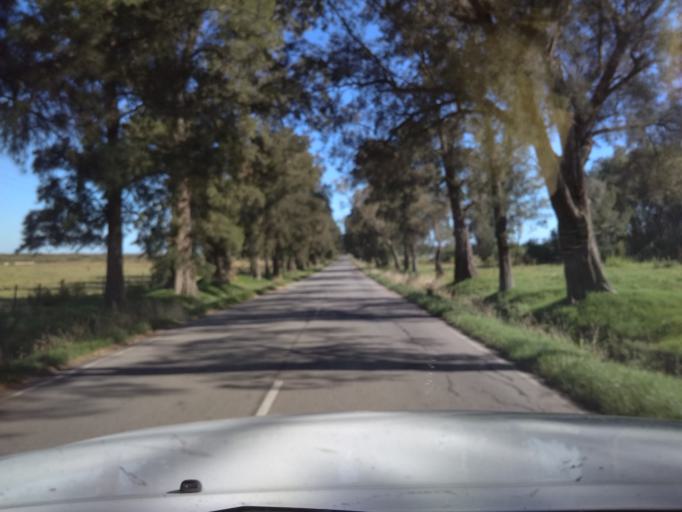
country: UY
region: Canelones
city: San Bautista
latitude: -34.3895
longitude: -55.9595
